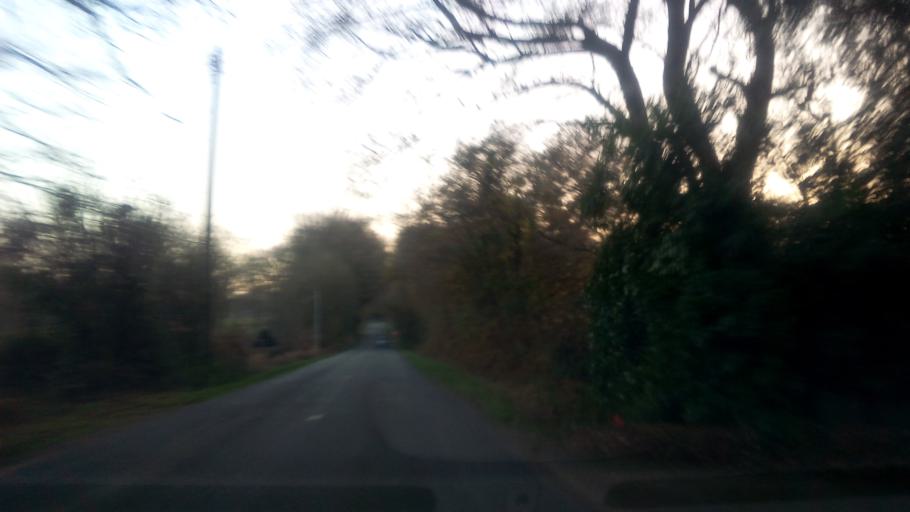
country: FR
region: Brittany
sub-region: Departement d'Ille-et-Vilaine
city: Bains-sur-Oust
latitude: 47.7159
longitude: -2.0538
